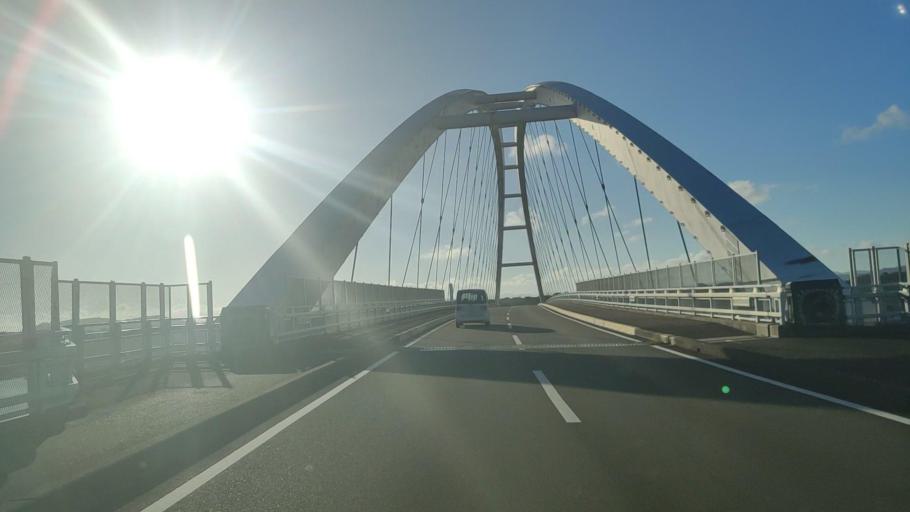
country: JP
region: Mie
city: Toba
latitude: 34.2649
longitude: 136.8154
